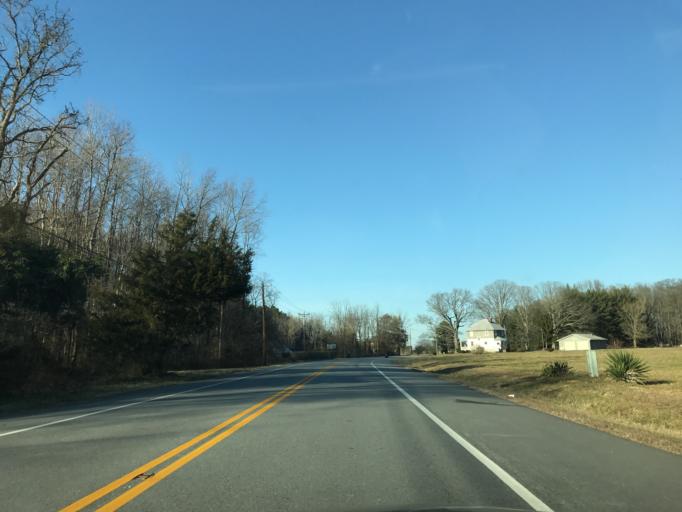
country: US
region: Maryland
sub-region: Queen Anne's County
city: Kingstown
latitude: 39.2359
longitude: -75.8740
